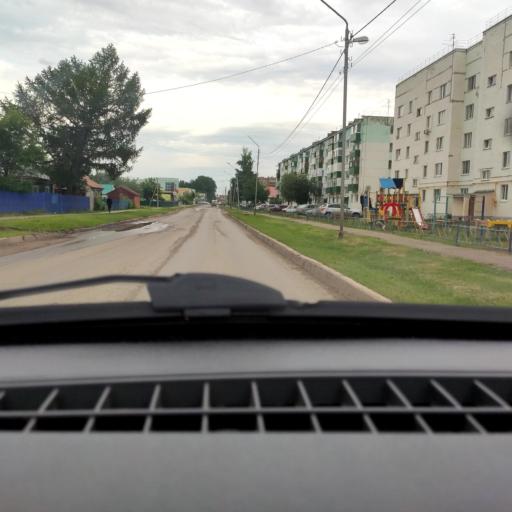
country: RU
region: Bashkortostan
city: Chishmy
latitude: 54.5890
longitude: 55.3897
